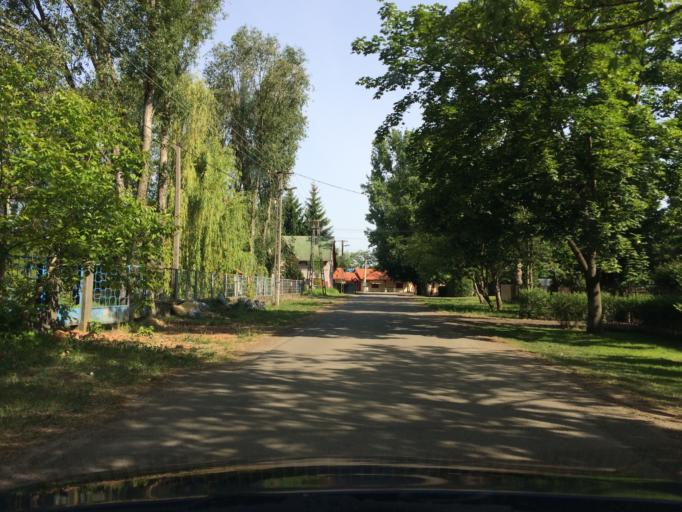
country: HU
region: Szabolcs-Szatmar-Bereg
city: Tiszavasvari
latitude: 47.9563
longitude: 21.3470
